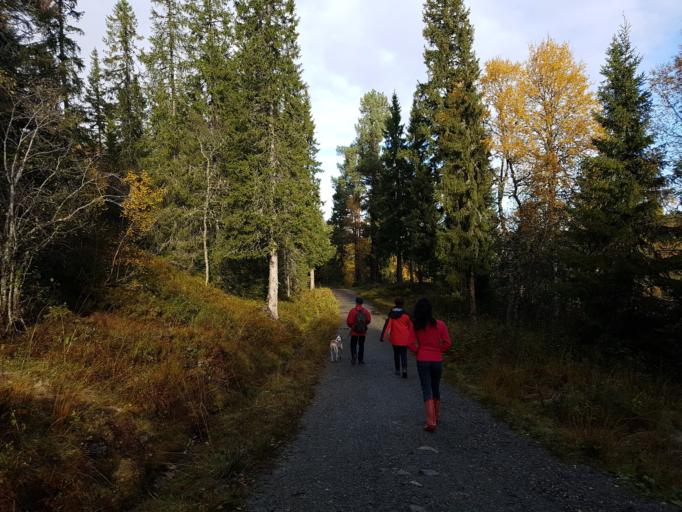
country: NO
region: Sor-Trondelag
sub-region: Trondheim
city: Trondheim
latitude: 63.4206
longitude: 10.2823
